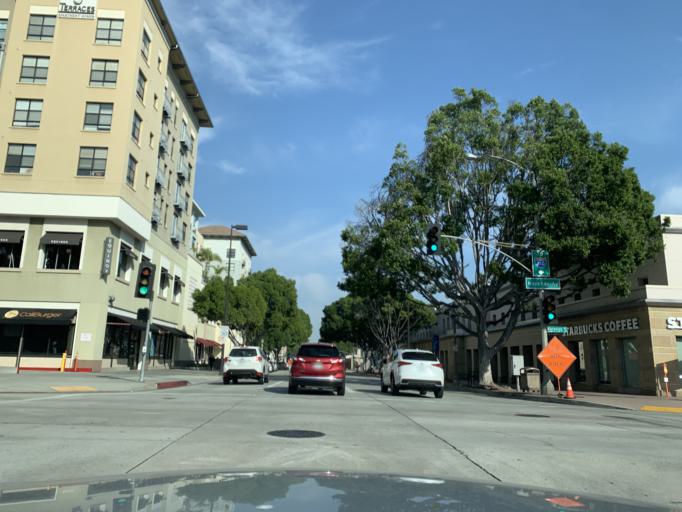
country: US
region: California
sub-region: Los Angeles County
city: Pasadena
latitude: 34.1446
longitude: -118.1460
